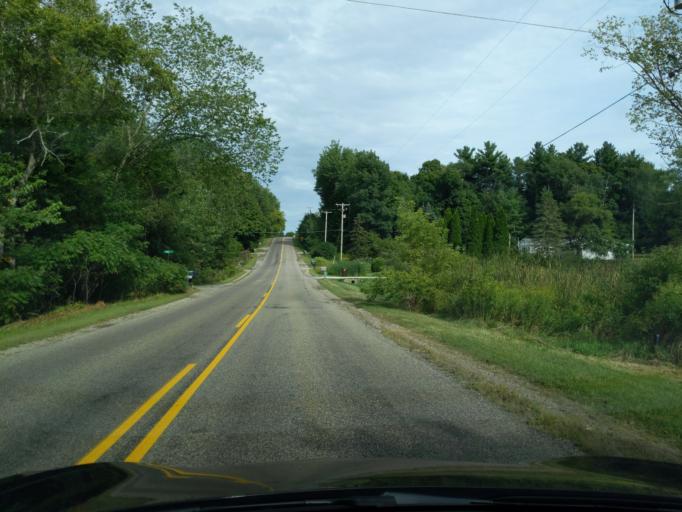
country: US
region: Michigan
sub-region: Eaton County
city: Dimondale
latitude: 42.6691
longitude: -84.6406
